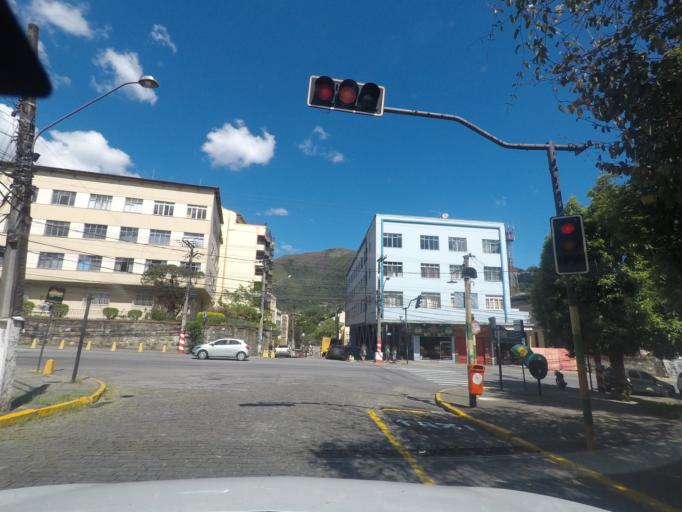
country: BR
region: Rio de Janeiro
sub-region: Teresopolis
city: Teresopolis
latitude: -22.4353
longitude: -42.9788
